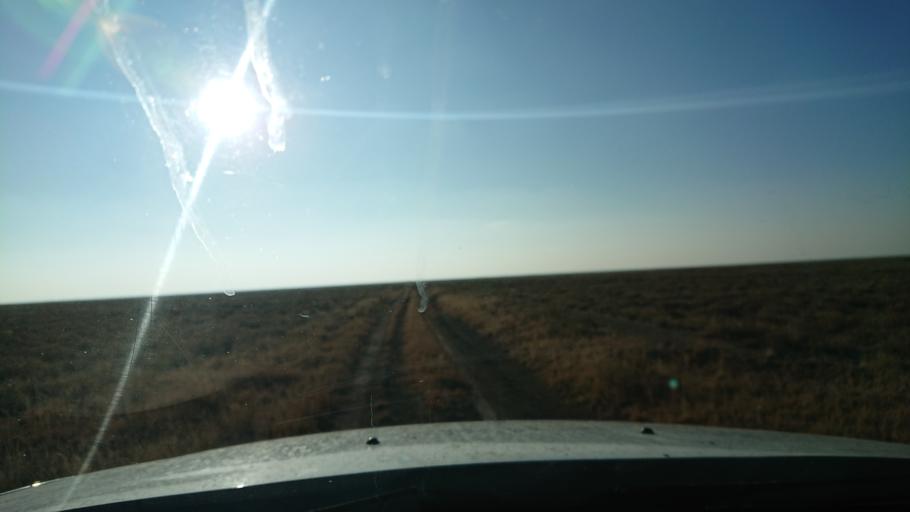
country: TR
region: Aksaray
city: Sultanhani
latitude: 38.3829
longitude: 33.5819
